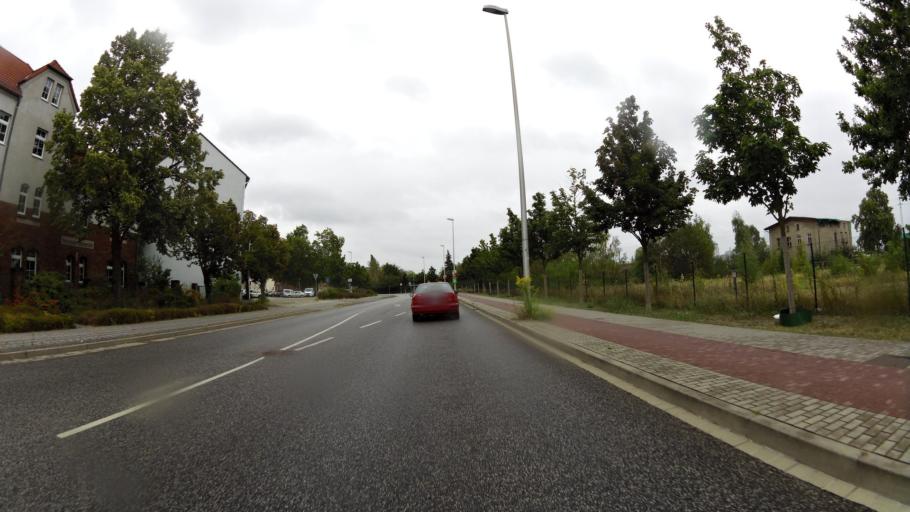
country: DE
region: Brandenburg
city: Cottbus
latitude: 51.7540
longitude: 14.3213
